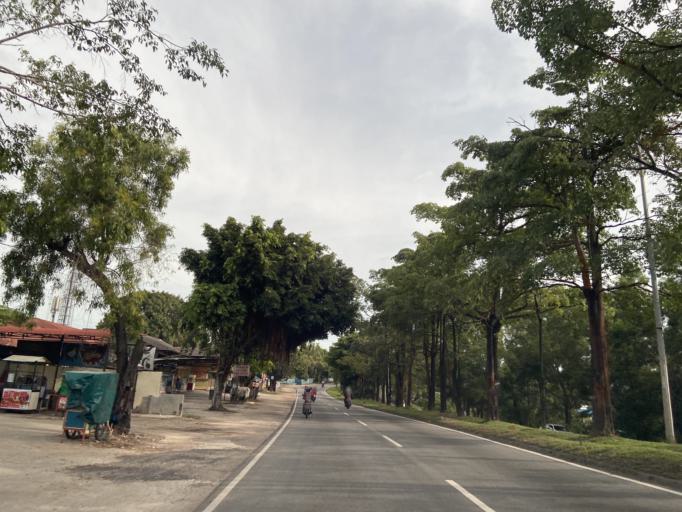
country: SG
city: Singapore
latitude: 1.1432
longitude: 104.0227
